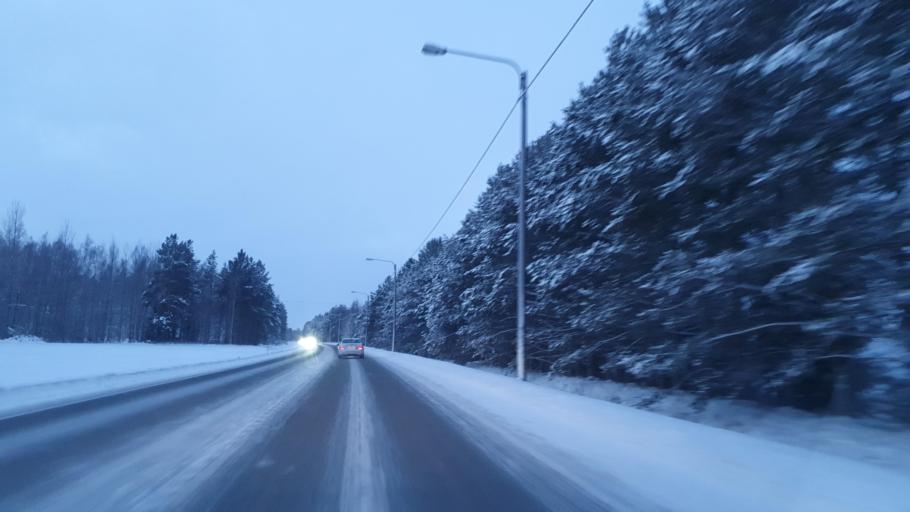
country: FI
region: Northern Ostrobothnia
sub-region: Oulu
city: Muhos
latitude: 64.8640
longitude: 25.8842
